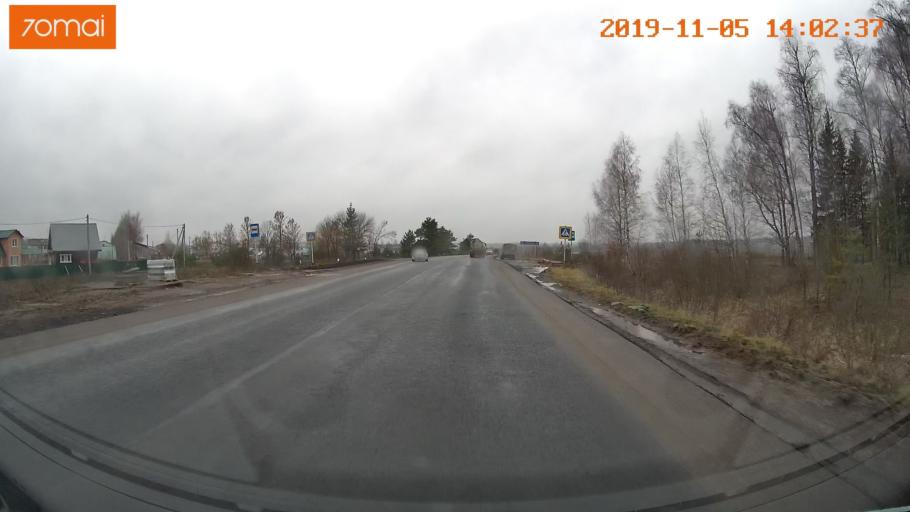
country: RU
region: Ivanovo
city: Kokhma
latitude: 57.0006
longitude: 41.2104
